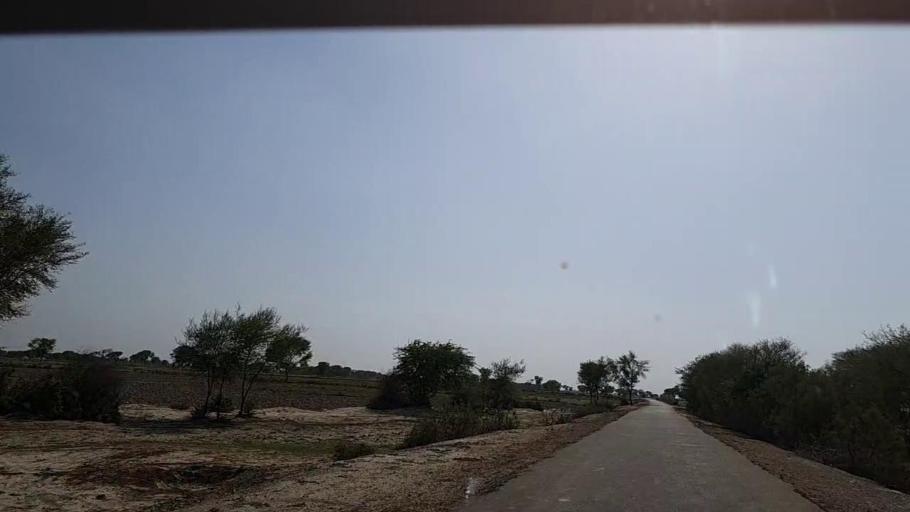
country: PK
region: Sindh
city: Phulji
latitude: 26.9245
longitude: 67.6817
